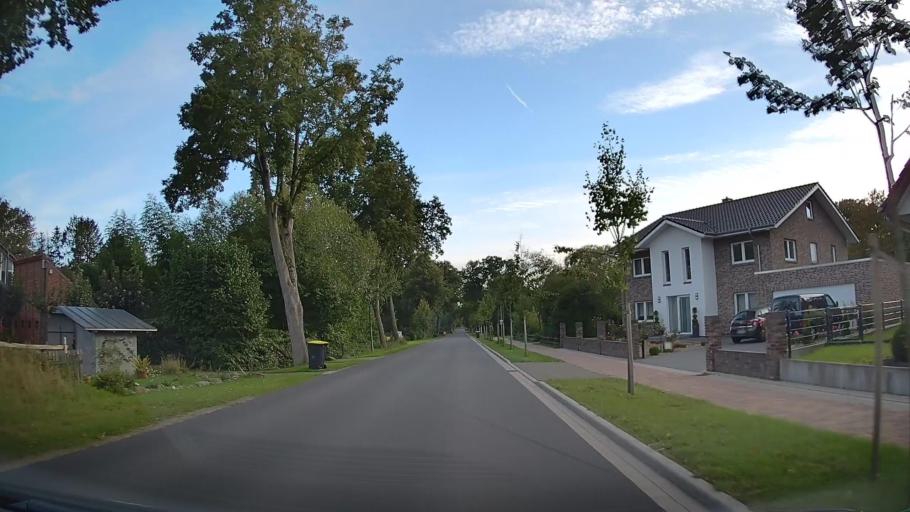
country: DE
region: Lower Saxony
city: Hassendorf
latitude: 53.1117
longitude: 9.2679
